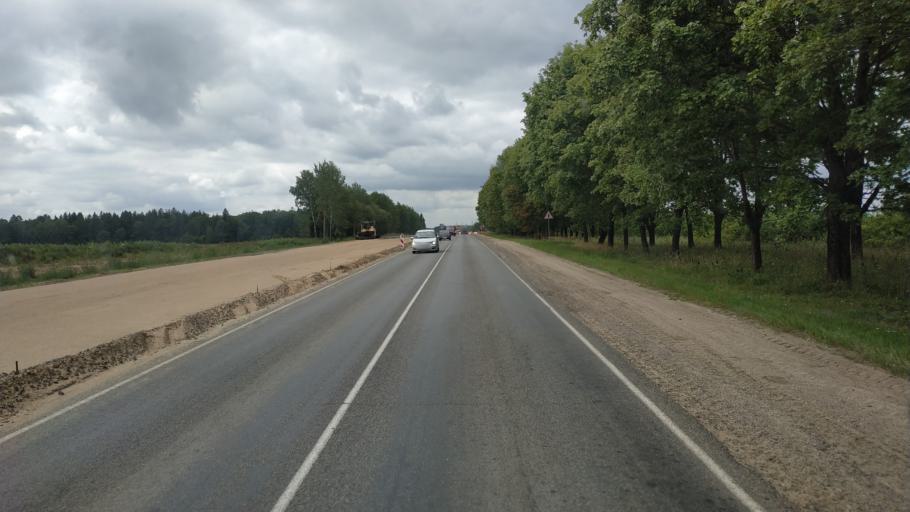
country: BY
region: Mogilev
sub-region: Mahilyowski Rayon
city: Kadino
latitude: 53.8700
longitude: 30.4622
